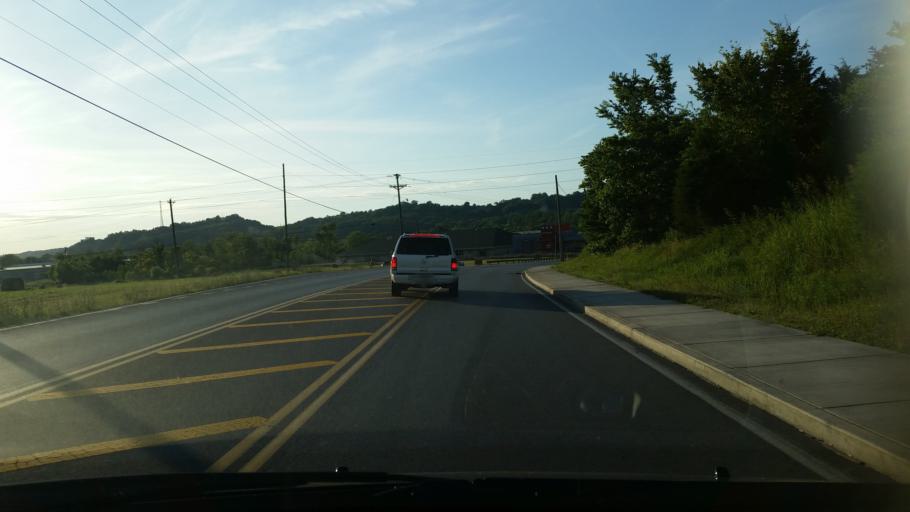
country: US
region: Tennessee
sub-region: Sevier County
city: Sevierville
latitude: 35.8614
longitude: -83.5460
